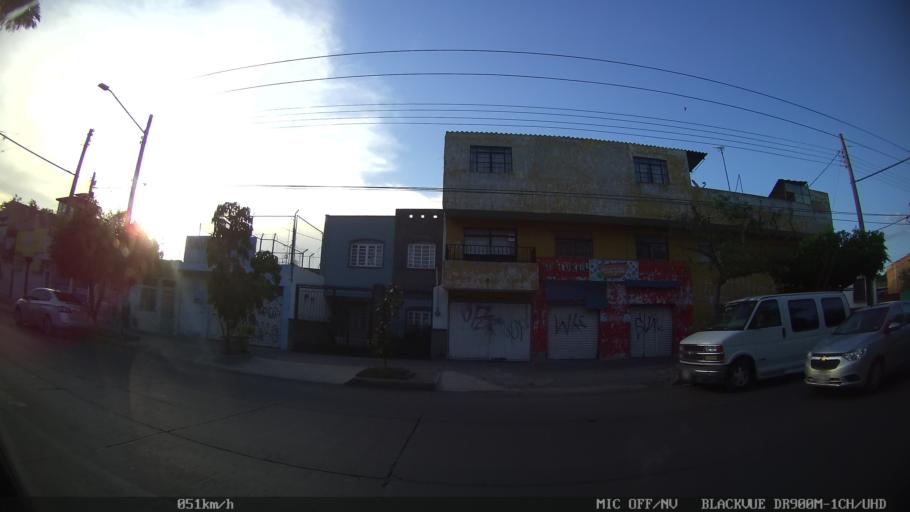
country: MX
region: Jalisco
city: Tlaquepaque
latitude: 20.6945
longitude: -103.3049
